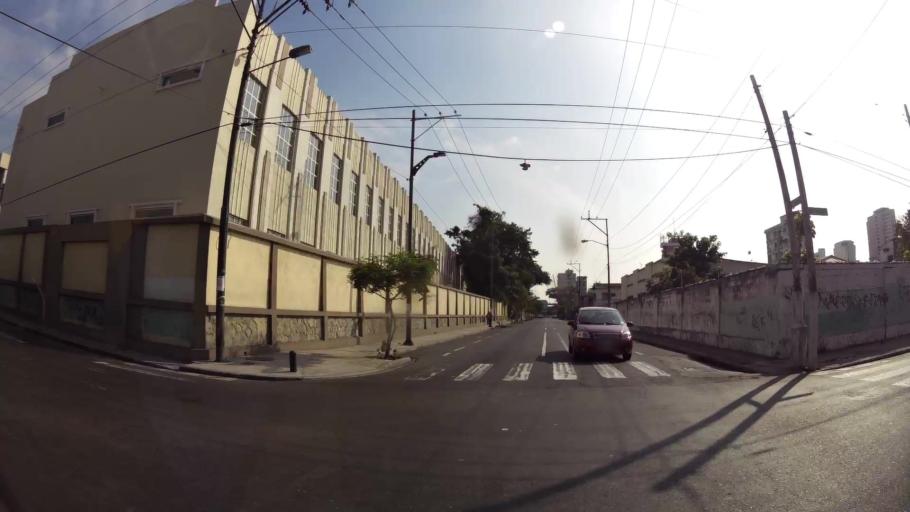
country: EC
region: Guayas
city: Guayaquil
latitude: -2.1903
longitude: -79.8979
